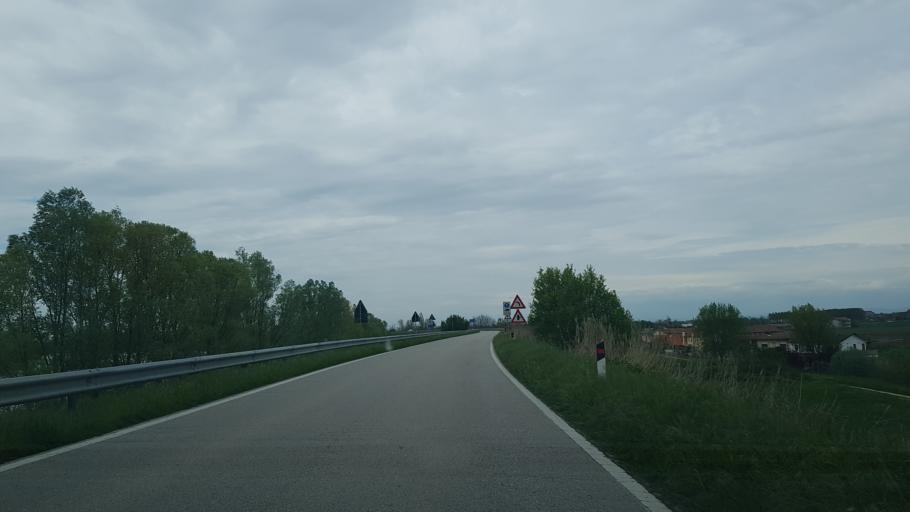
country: IT
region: Veneto
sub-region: Provincia di Rovigo
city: Lusia
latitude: 45.1066
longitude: 11.6552
